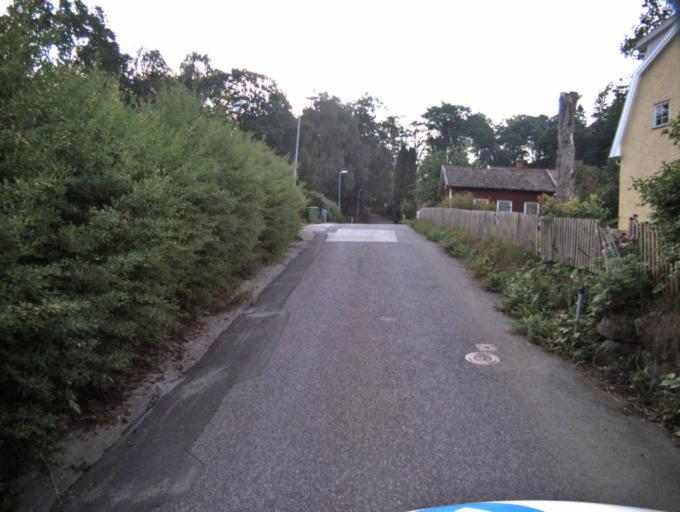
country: SE
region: Vaestra Goetaland
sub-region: Ulricehamns Kommun
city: Ulricehamn
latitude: 57.8025
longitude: 13.4211
